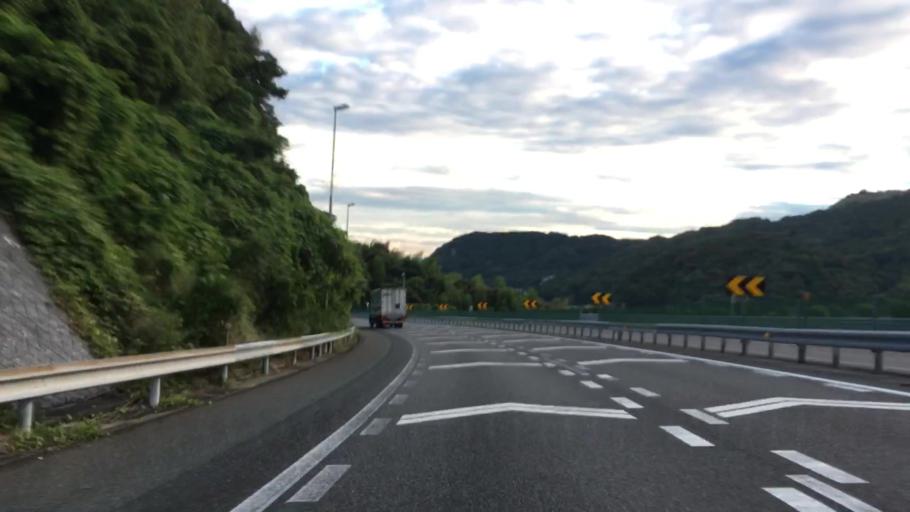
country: JP
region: Yamaguchi
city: Shimonoseki
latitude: 34.0350
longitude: 130.9636
